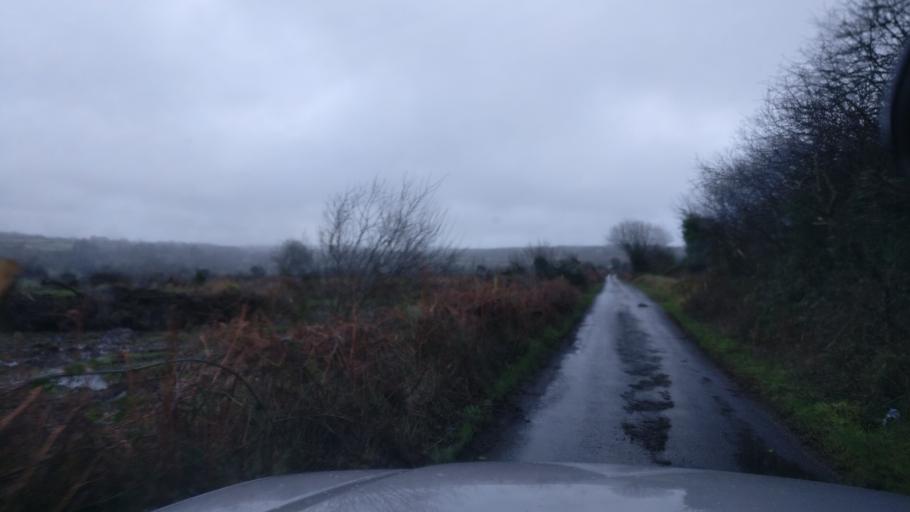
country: IE
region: Connaught
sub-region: County Galway
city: Loughrea
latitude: 53.1523
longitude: -8.6323
